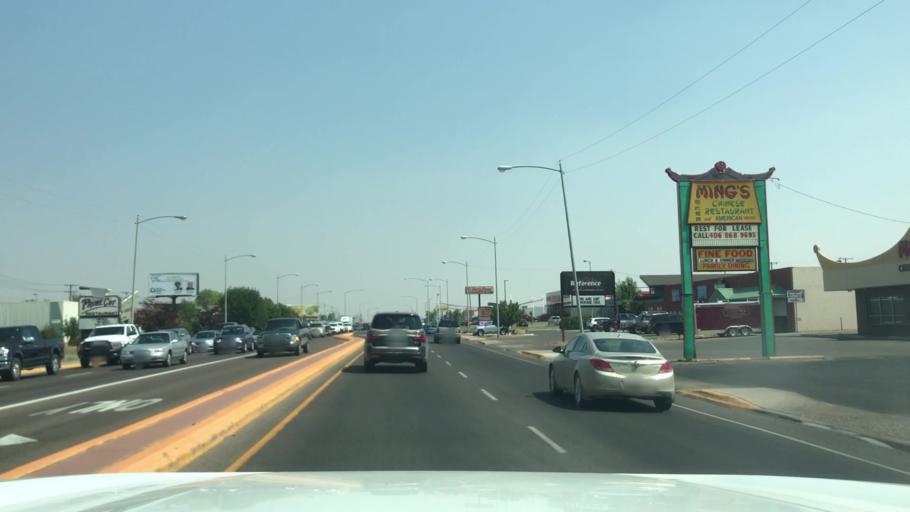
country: US
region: Montana
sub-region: Cascade County
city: Great Falls
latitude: 47.4940
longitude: -111.2518
